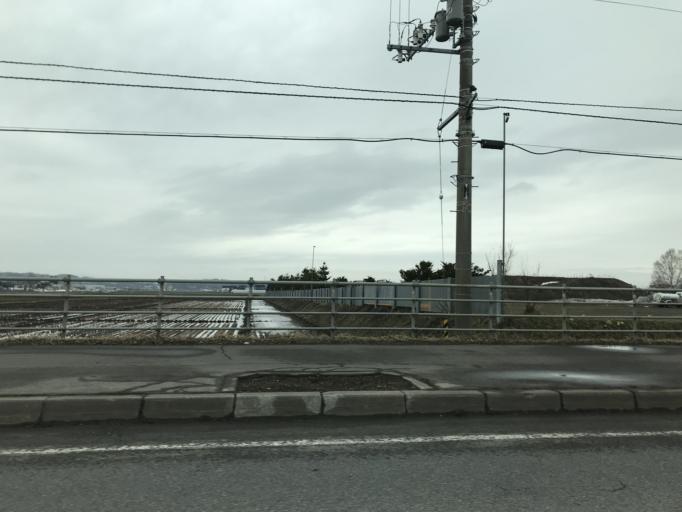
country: JP
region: Hokkaido
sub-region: Asahikawa-shi
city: Asahikawa
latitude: 43.8201
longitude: 142.4095
